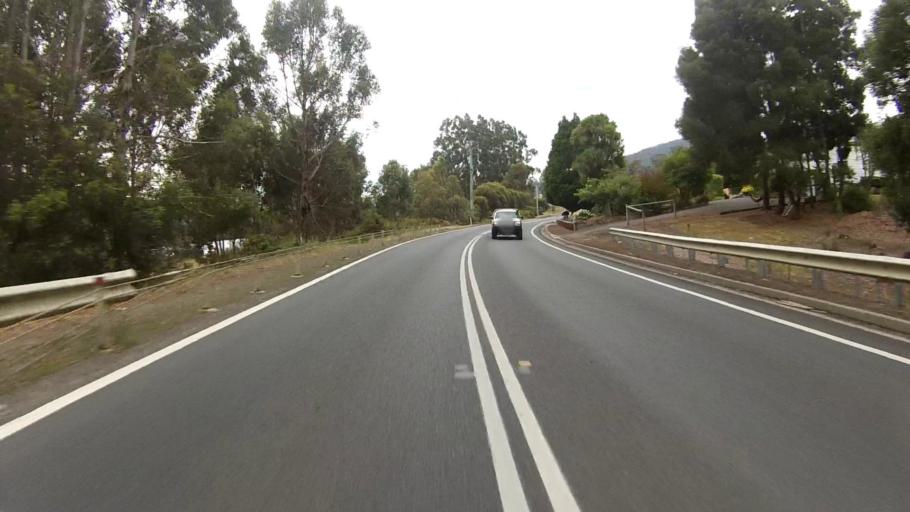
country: AU
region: Tasmania
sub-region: Huon Valley
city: Franklin
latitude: -43.0767
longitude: 147.0332
